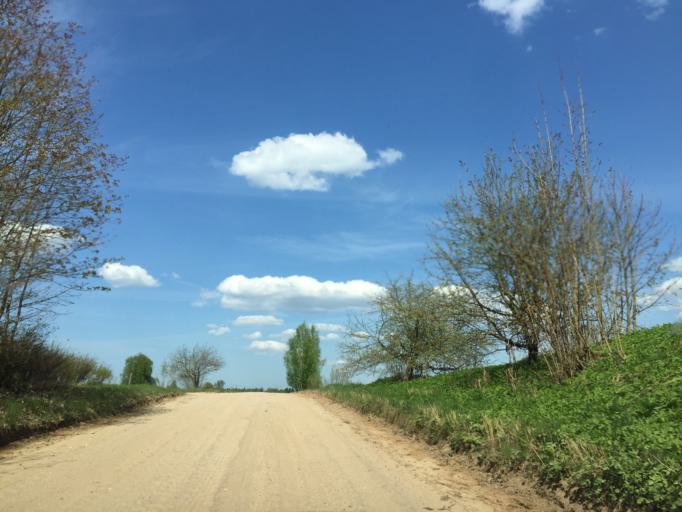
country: LV
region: Krimulda
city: Ragana
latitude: 57.3481
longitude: 24.6513
